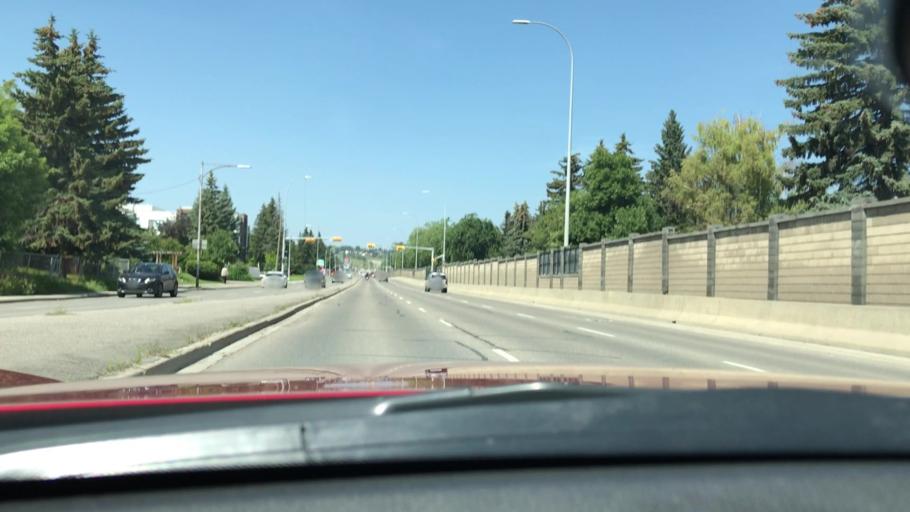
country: CA
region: Alberta
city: Calgary
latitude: 51.0465
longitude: -114.1453
